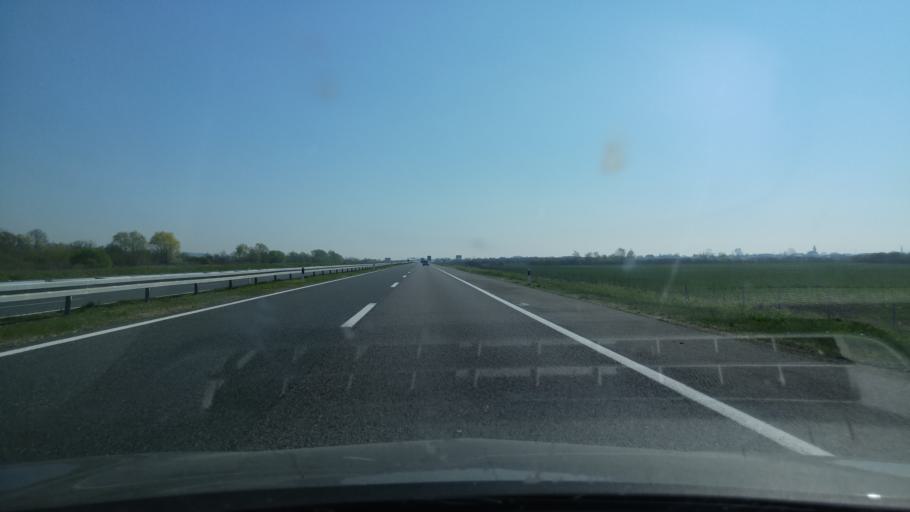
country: HR
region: Brodsko-Posavska
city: Slobodnica
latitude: 45.1692
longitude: 17.9114
